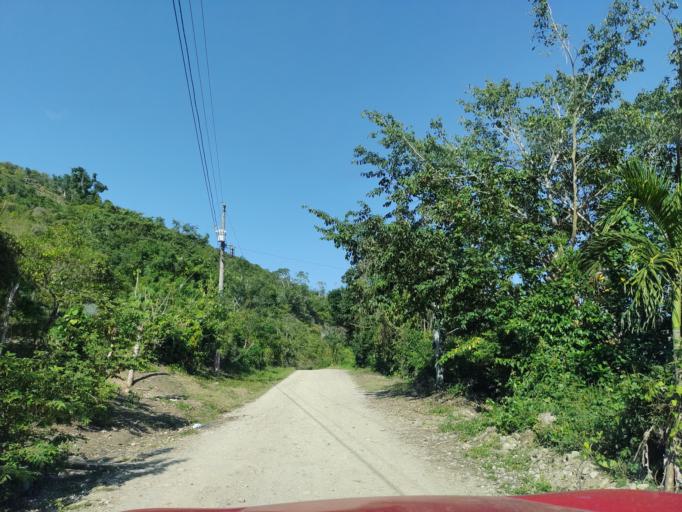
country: MX
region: Veracruz
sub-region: Papantla
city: Polutla
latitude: 20.4986
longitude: -97.1781
